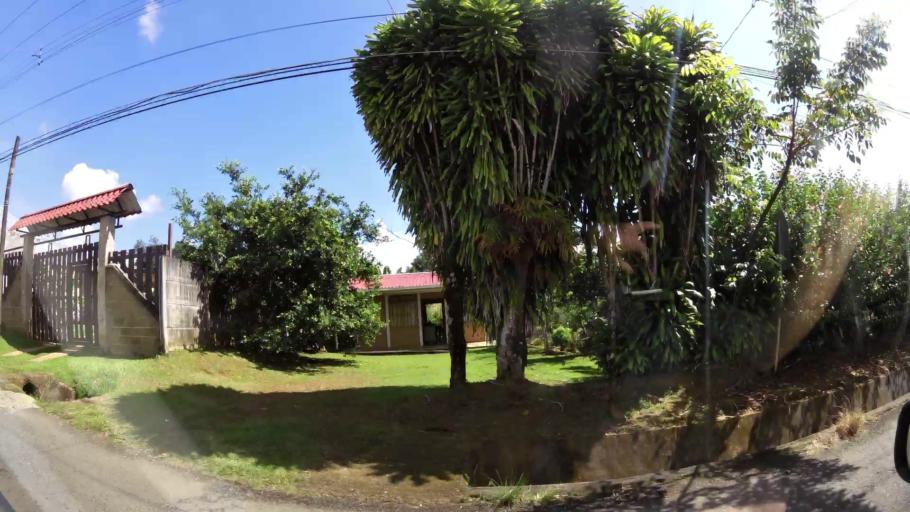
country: CR
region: San Jose
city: San Isidro
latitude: 9.3830
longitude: -83.6976
